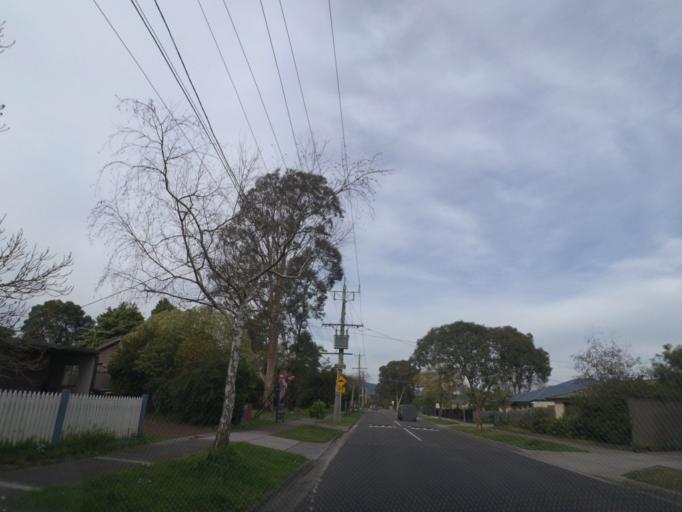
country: AU
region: Victoria
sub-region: Knox
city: Knoxfield
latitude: -37.8887
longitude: 145.2539
